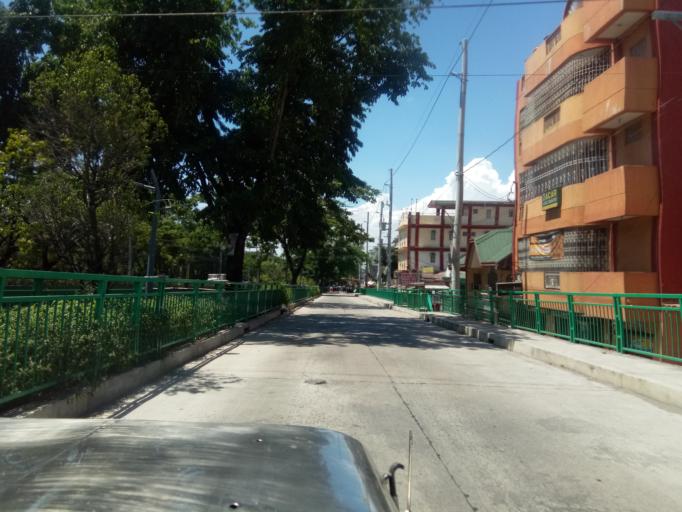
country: PH
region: Calabarzon
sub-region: Province of Cavite
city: Dasmarinas
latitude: 14.3203
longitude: 120.9639
